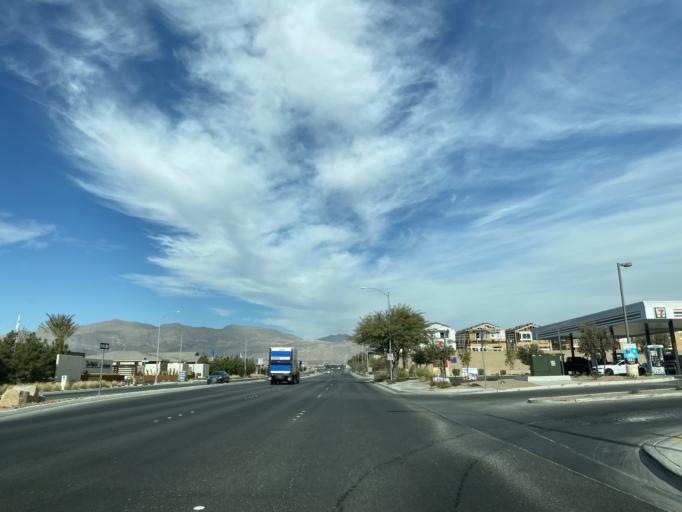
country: US
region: Nevada
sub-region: Clark County
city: Nellis Air Force Base
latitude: 36.2790
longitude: -115.1168
